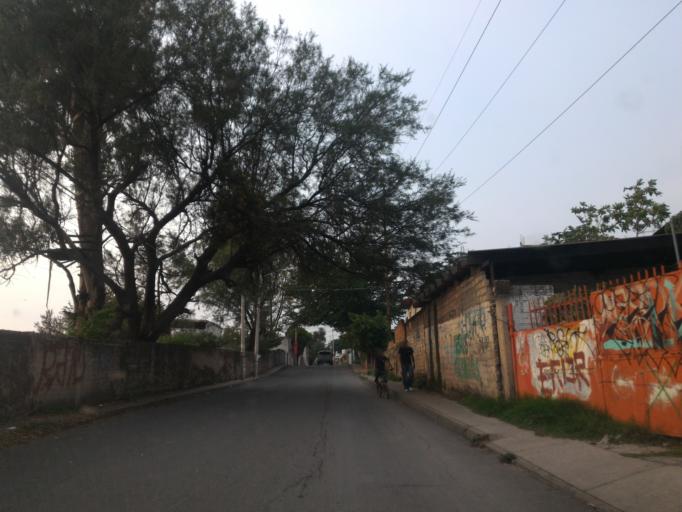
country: MX
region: Jalisco
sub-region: San Pedro Tlaquepaque
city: Paseo del Prado
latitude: 20.5891
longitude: -103.3898
